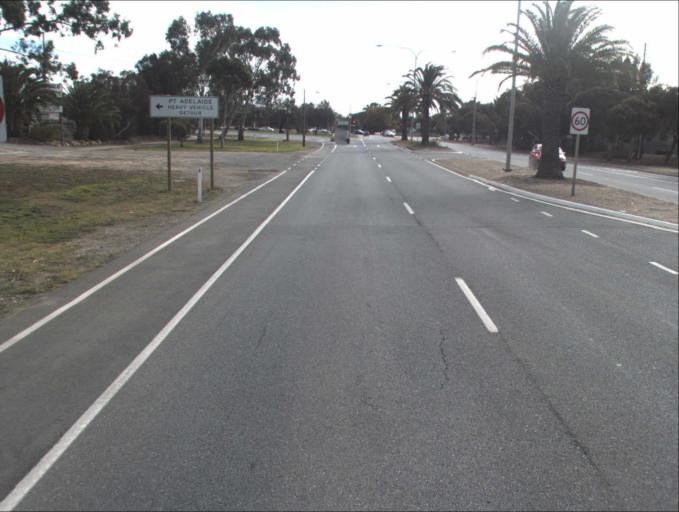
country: AU
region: South Australia
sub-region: Charles Sturt
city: West Lakes Shore
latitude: -34.8548
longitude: 138.5022
